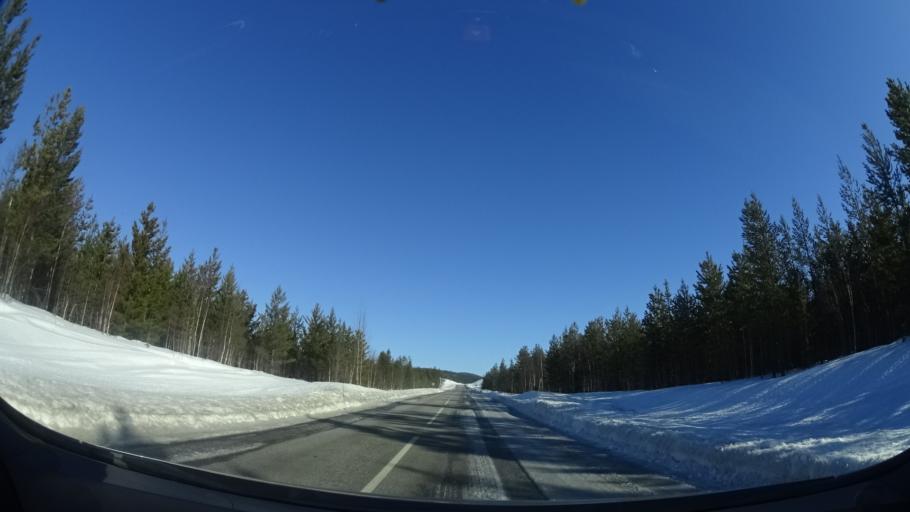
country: SE
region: Vaesterbotten
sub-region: Skelleftea Kommun
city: Langsele
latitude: 65.1115
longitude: 20.0825
